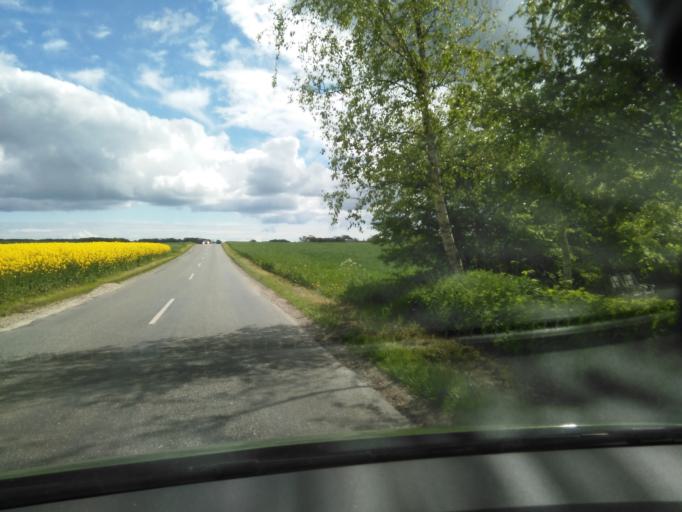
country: DK
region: Central Jutland
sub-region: Arhus Kommune
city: Solbjerg
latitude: 56.0725
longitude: 10.0936
